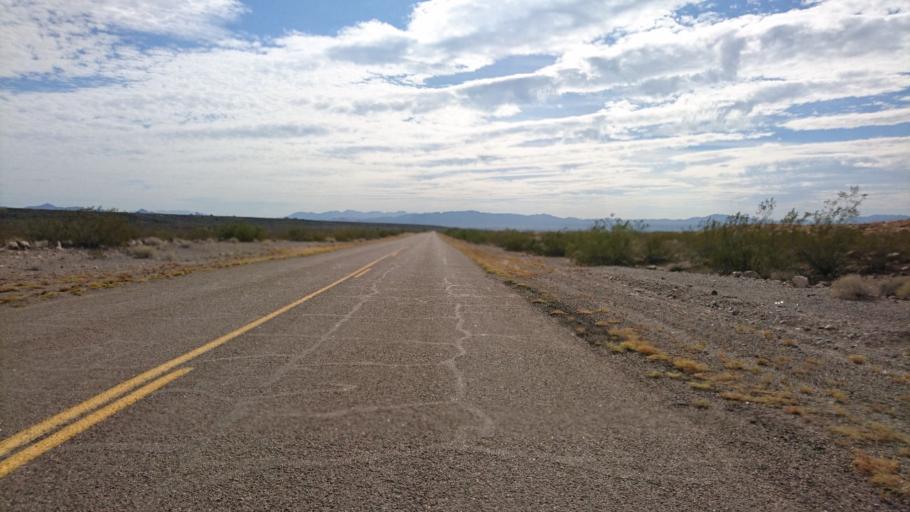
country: US
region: Arizona
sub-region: Mohave County
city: Mohave Valley
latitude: 34.8685
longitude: -114.4407
